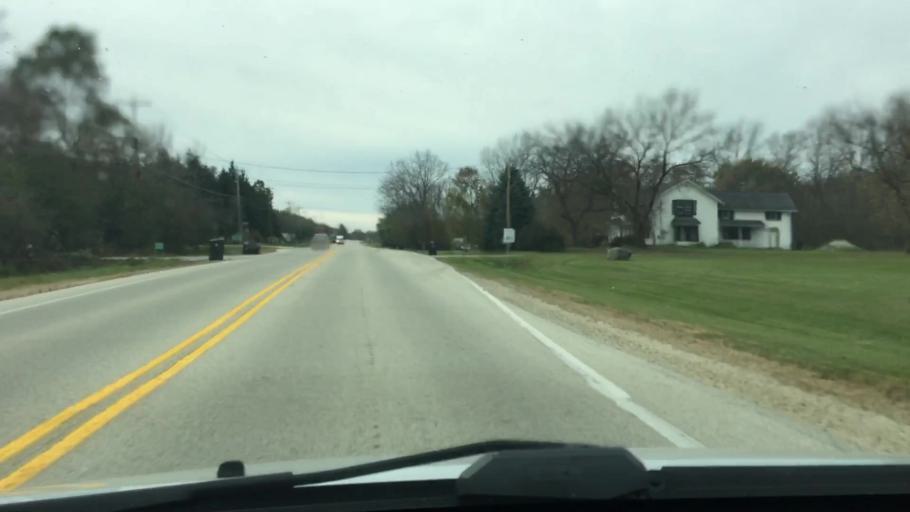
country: US
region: Wisconsin
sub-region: Waukesha County
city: Mukwonago
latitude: 42.8965
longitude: -88.2729
